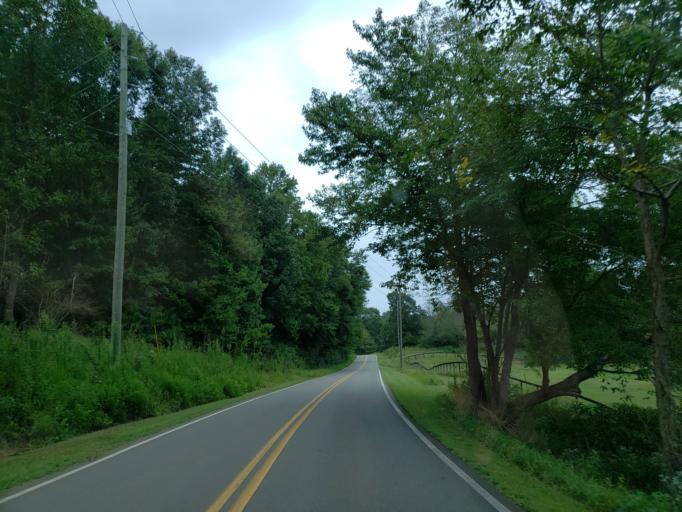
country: US
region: Georgia
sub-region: Pickens County
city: Jasper
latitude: 34.4145
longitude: -84.5706
